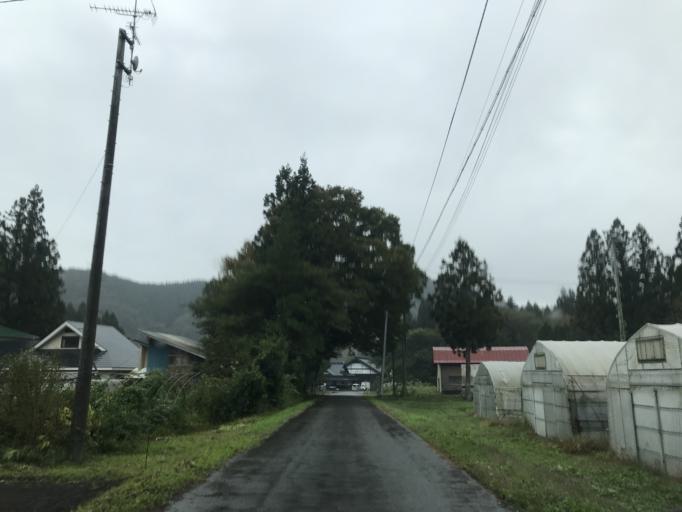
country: JP
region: Iwate
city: Ichinoseki
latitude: 38.9738
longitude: 140.9595
